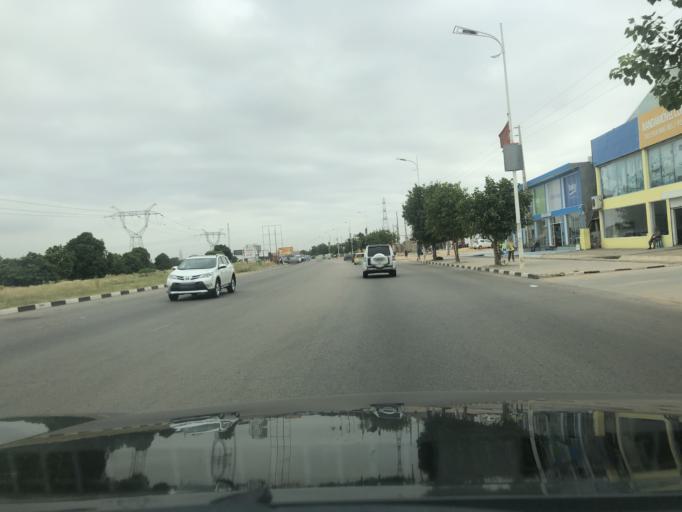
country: AO
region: Luanda
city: Luanda
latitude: -8.9782
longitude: 13.2898
